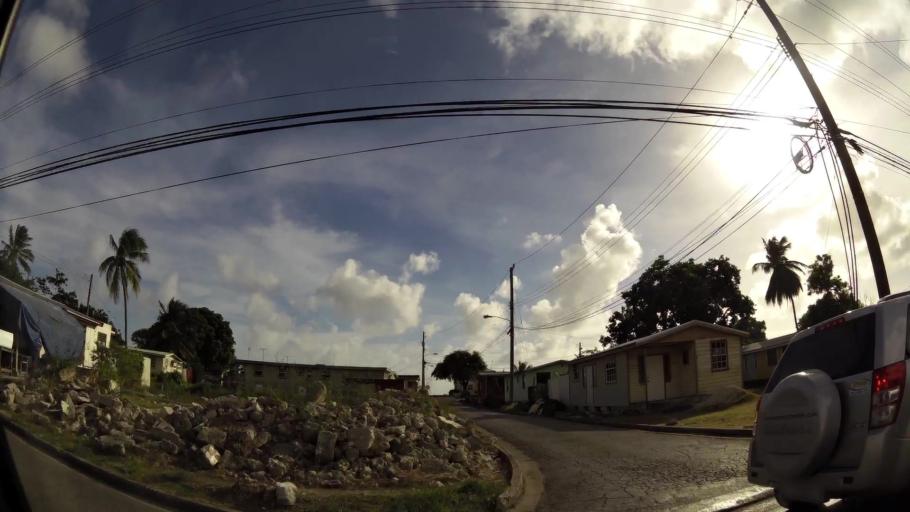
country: BB
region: Saint Michael
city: Bridgetown
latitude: 13.0867
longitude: -59.5807
